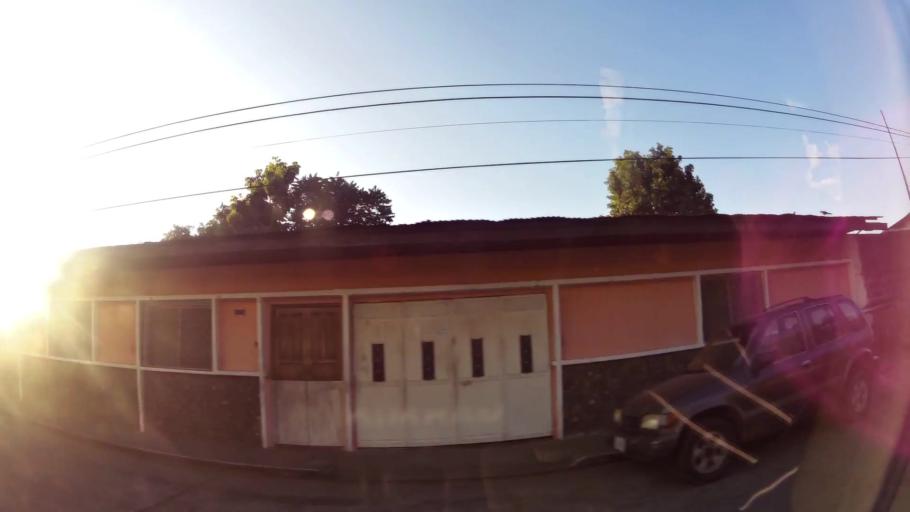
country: GT
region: Suchitepeque
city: Mazatenango
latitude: 14.5384
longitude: -91.5044
